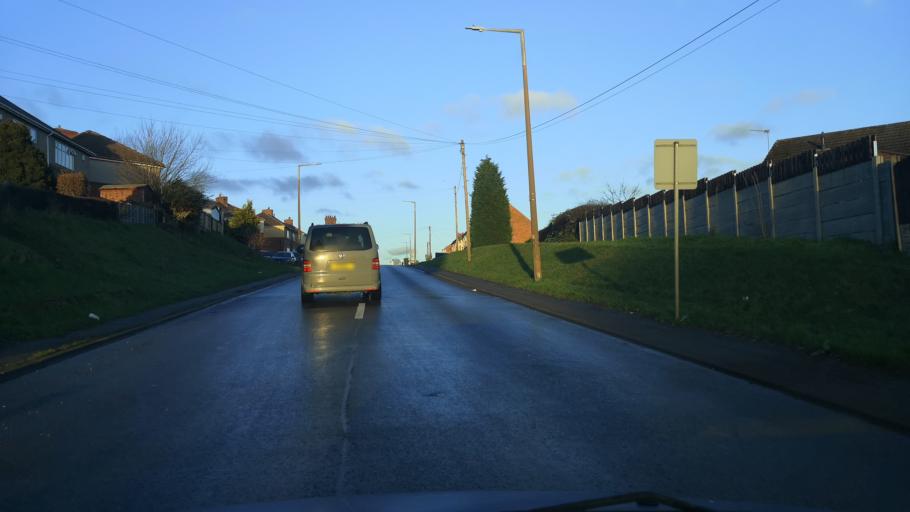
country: GB
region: England
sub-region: Barnsley
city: Little Houghton
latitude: 53.5396
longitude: -1.3514
